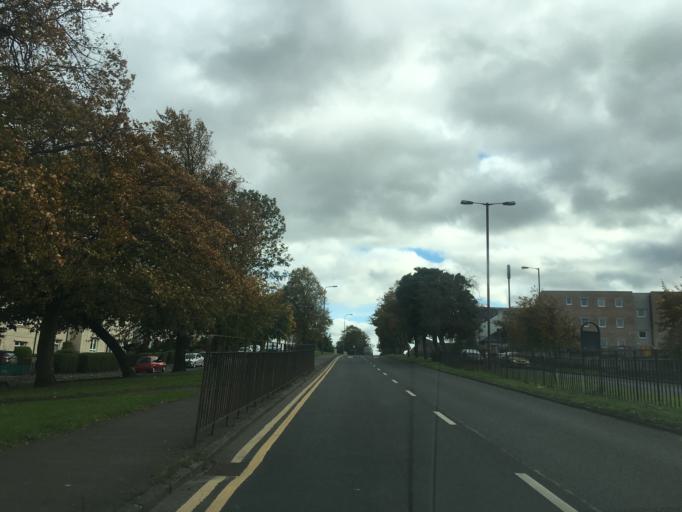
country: GB
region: Scotland
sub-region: Edinburgh
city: Edinburgh
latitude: 55.9715
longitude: -3.2520
